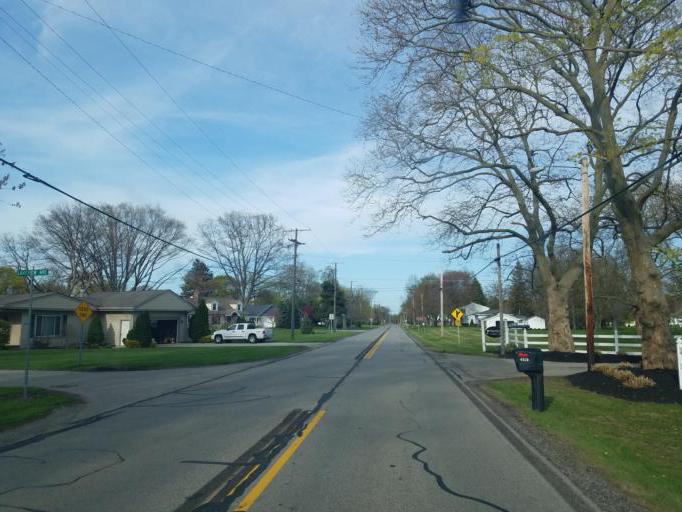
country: US
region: Ohio
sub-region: Ashtabula County
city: Ashtabula
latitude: 41.8868
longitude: -80.8444
